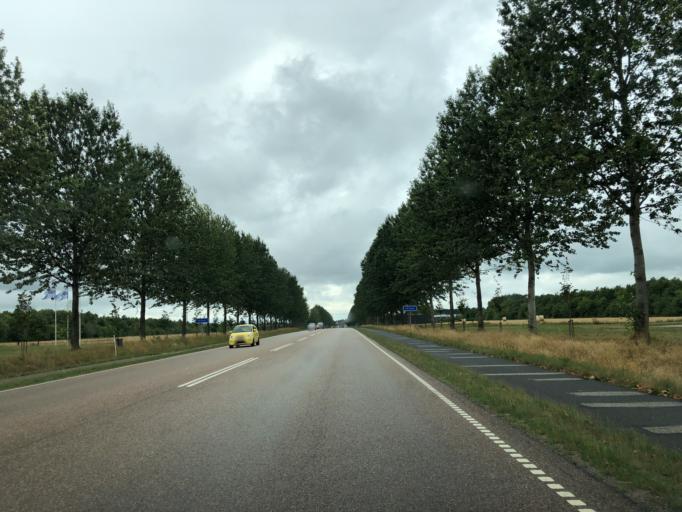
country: DK
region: Central Jutland
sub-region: Herning Kommune
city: Hammerum
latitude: 56.1357
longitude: 9.1040
